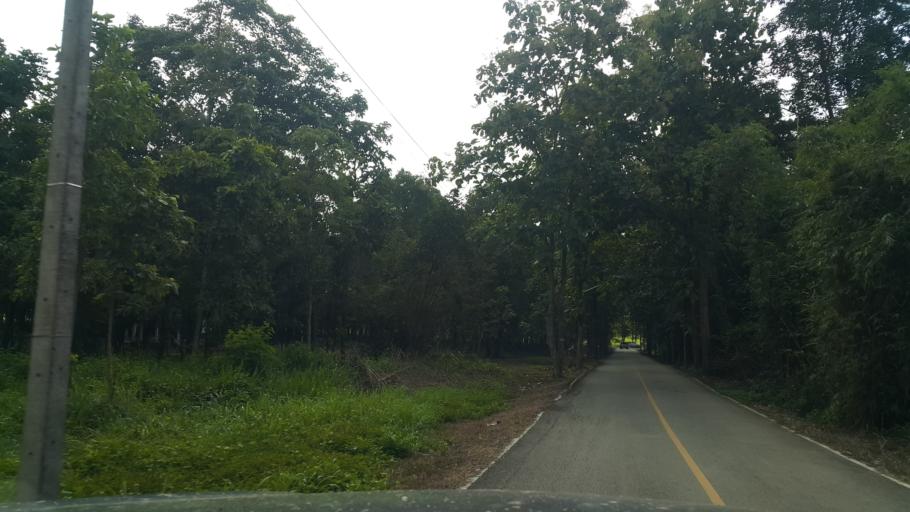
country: TH
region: Chiang Mai
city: Mae On
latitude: 18.7454
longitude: 99.2218
